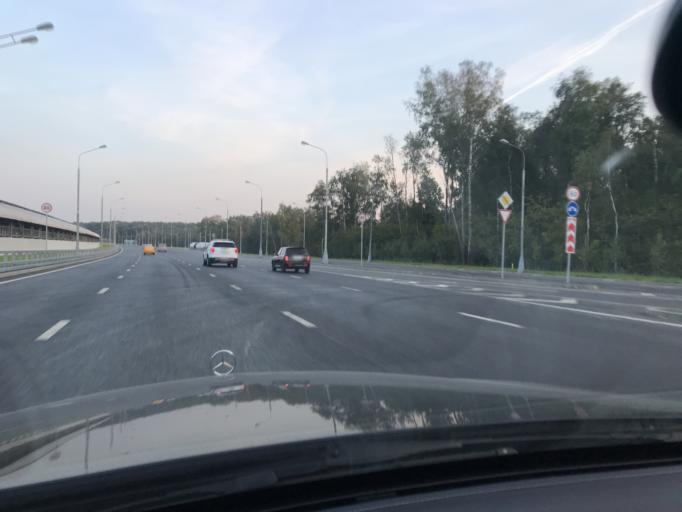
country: RU
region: Moskovskaya
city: Mosrentgen
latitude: 55.5928
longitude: 37.4202
